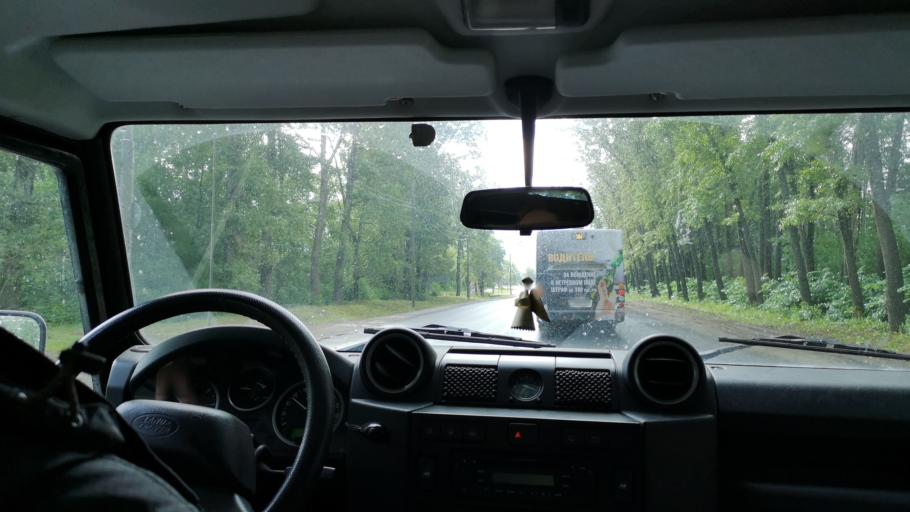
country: RU
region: Moskovskaya
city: Gorshkovo
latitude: 56.3670
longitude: 37.4635
